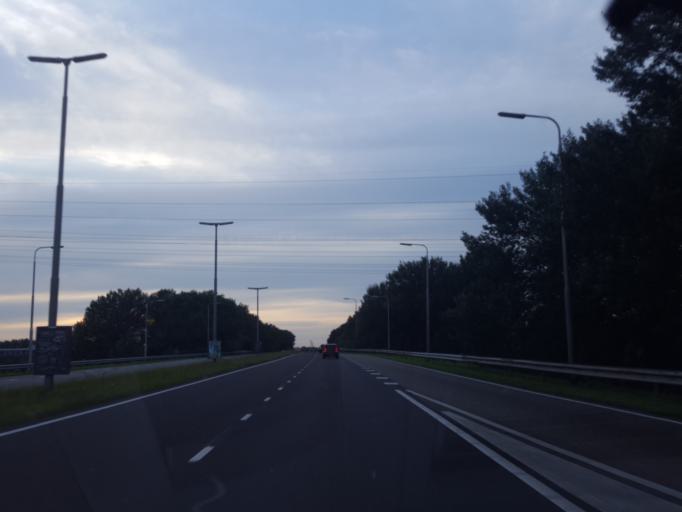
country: NL
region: Friesland
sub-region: Gemeente Leeuwarden
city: Camminghaburen
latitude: 53.1999
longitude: 5.8378
